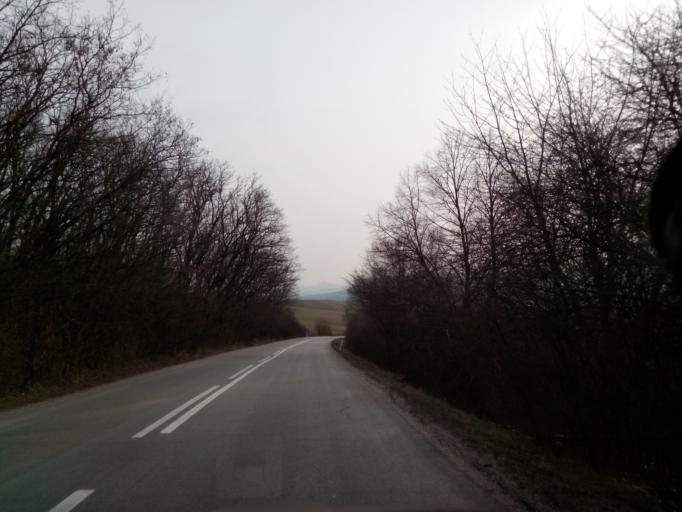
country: SK
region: Kosicky
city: Secovce
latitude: 48.6287
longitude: 21.5541
